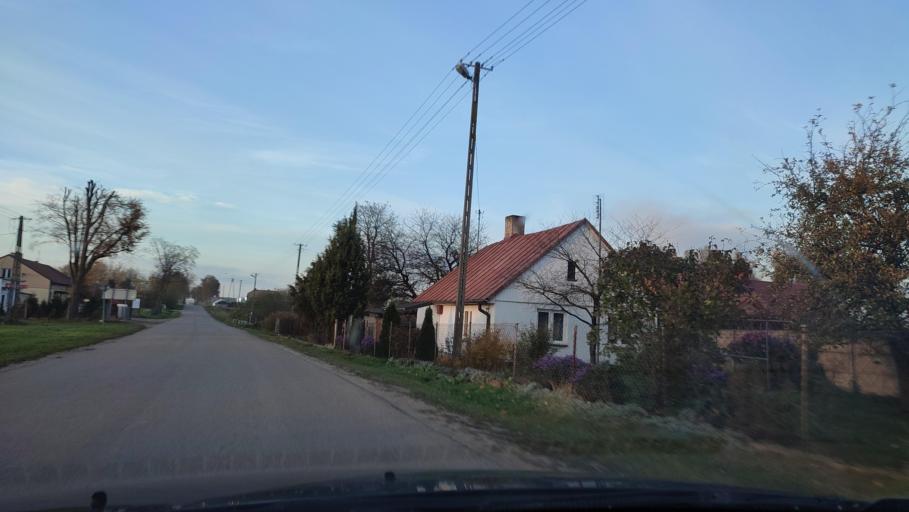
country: PL
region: Masovian Voivodeship
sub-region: Powiat mlawski
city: Wieczfnia Koscielna
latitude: 53.1894
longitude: 20.4396
